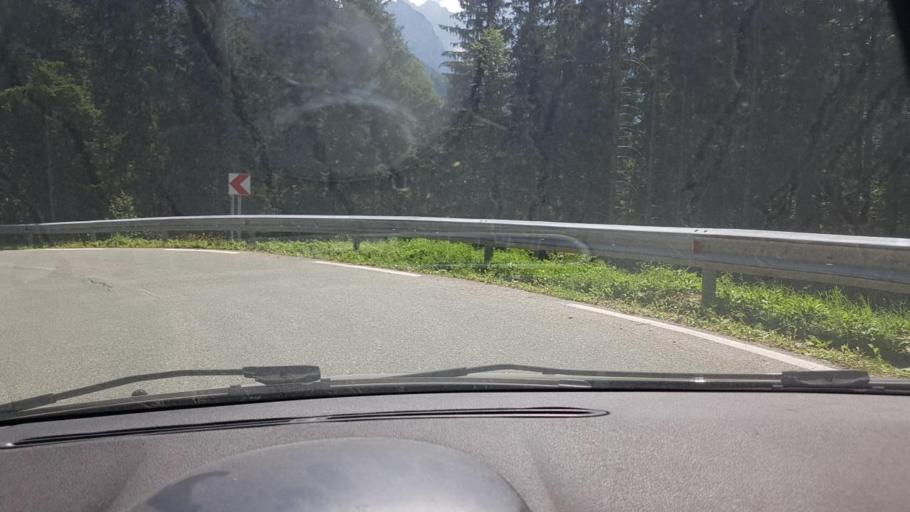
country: SI
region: Jezersko
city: Zgornje Jezersko
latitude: 46.4157
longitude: 14.5257
